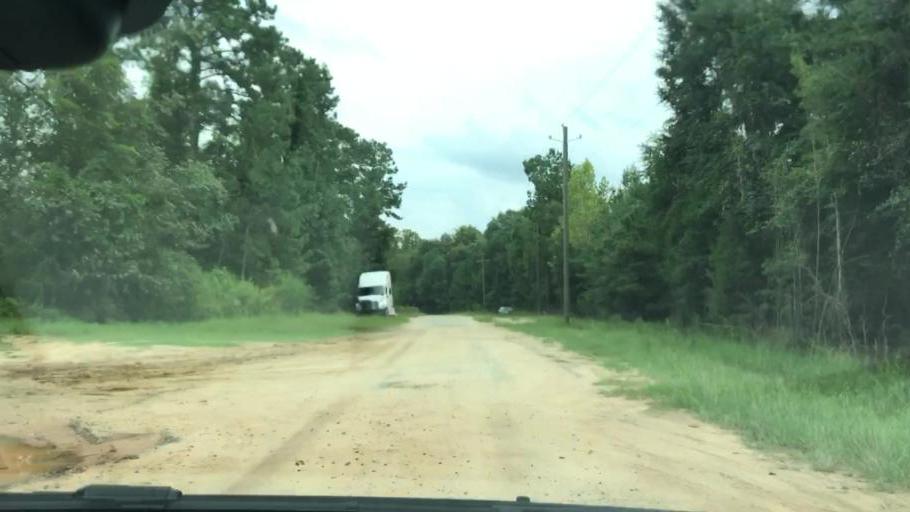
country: US
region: Georgia
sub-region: Clay County
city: Fort Gaines
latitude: 31.6274
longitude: -85.0492
